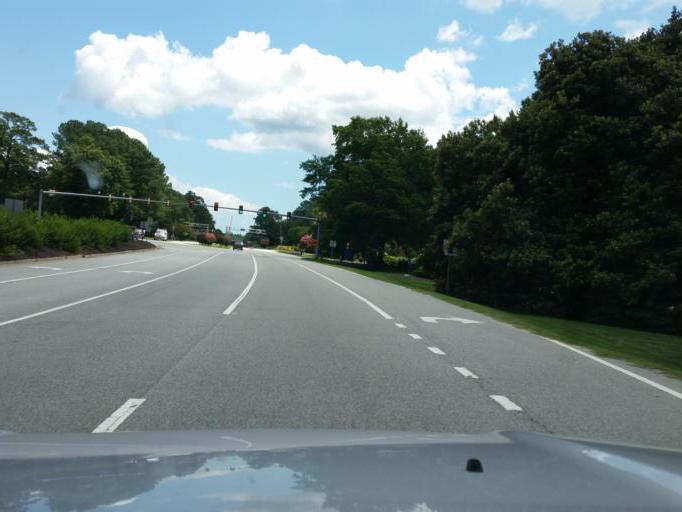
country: US
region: Virginia
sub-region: City of Williamsburg
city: Williamsburg
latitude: 37.2404
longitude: -76.6519
